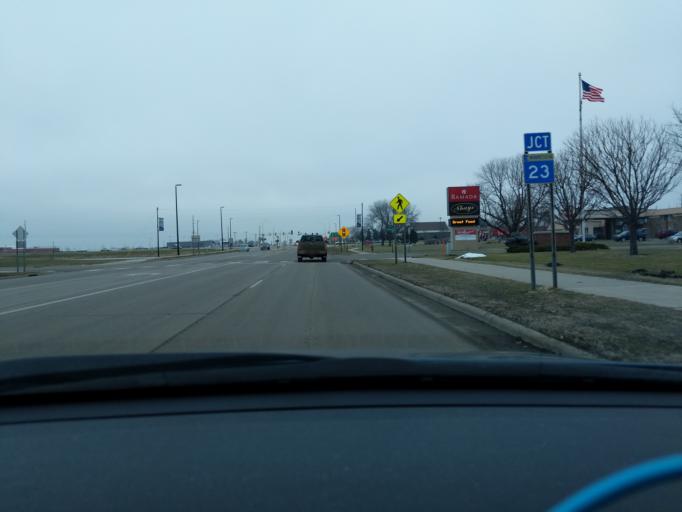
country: US
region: Minnesota
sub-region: Lyon County
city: Marshall
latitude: 44.4504
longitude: -95.7596
